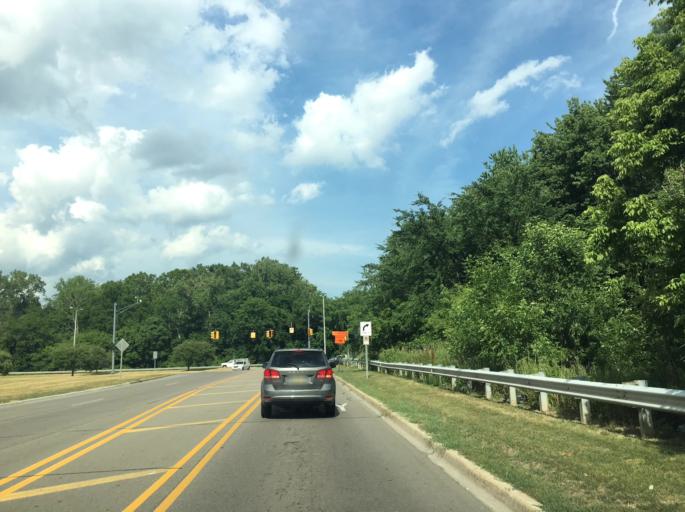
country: US
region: Michigan
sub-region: Macomb County
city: Sterling Heights
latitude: 42.5821
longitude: -82.9941
